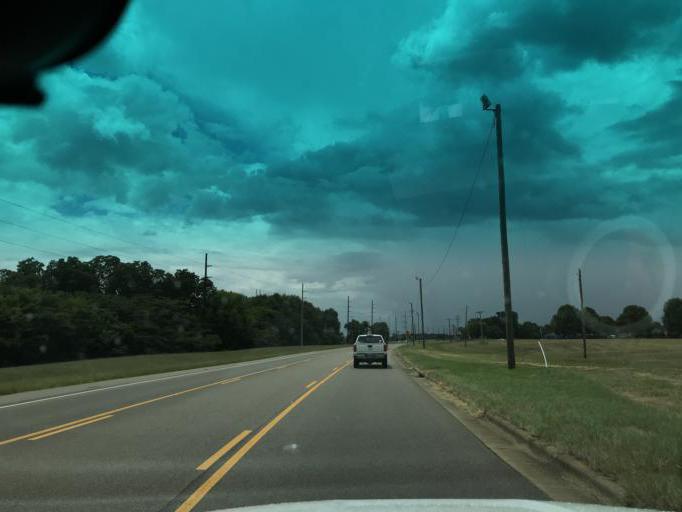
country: US
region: Alabama
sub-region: Montgomery County
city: Pike Road
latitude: 32.3689
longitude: -86.1354
